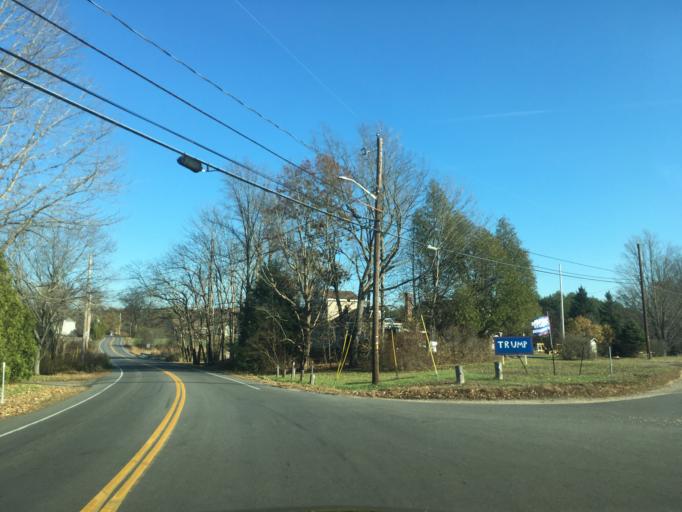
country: US
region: New Hampshire
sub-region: Rockingham County
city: Stratham Station
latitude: 43.0369
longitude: -70.9234
